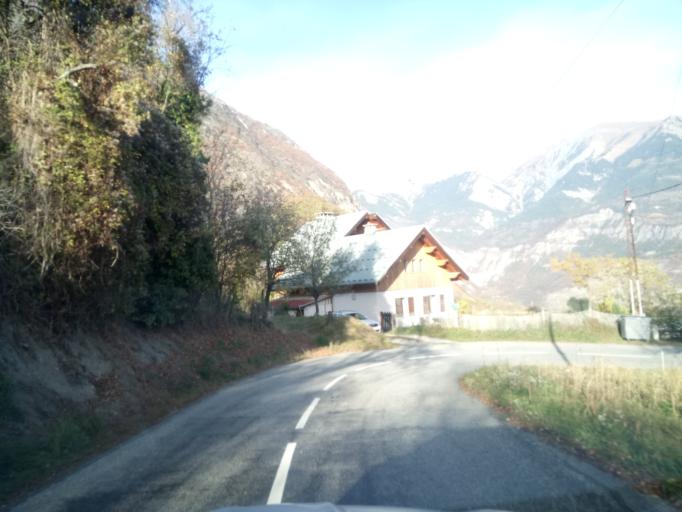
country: FR
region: Rhone-Alpes
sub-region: Departement de la Savoie
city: Saint-Jean-de-Maurienne
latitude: 45.2770
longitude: 6.3331
